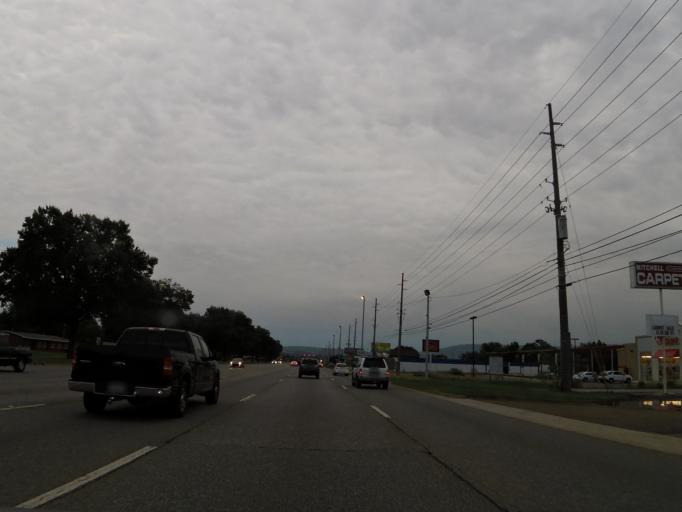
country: US
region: Alabama
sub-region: Madison County
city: Huntsville
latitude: 34.7358
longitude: -86.6099
